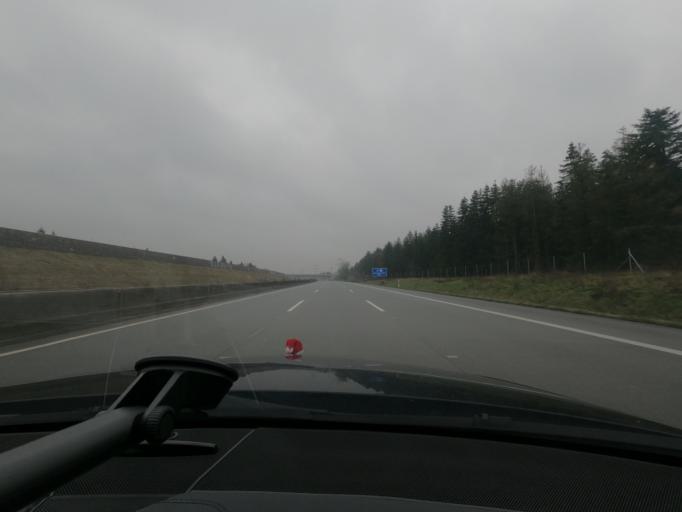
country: DE
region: Schleswig-Holstein
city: Kaltenkirchen
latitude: 53.8289
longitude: 9.9237
